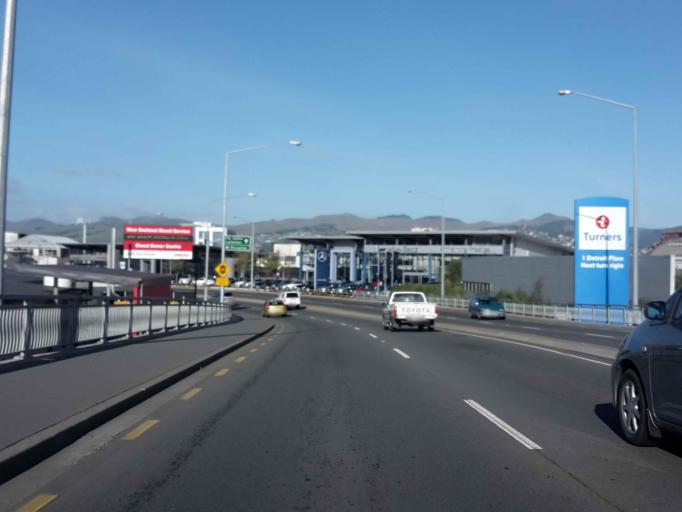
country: NZ
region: Canterbury
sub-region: Christchurch City
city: Christchurch
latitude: -43.5395
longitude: 172.6101
